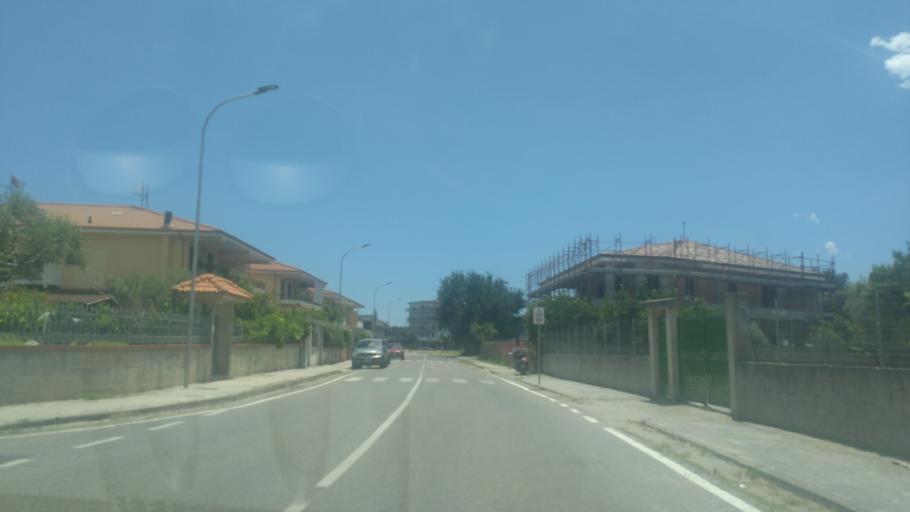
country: IT
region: Calabria
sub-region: Provincia di Catanzaro
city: Montepaone Lido
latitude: 38.7229
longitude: 16.5329
